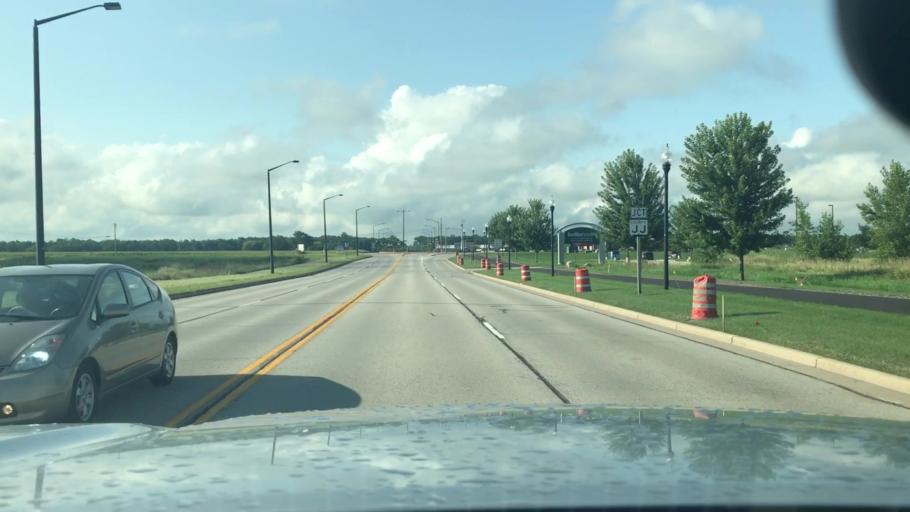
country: US
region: Wisconsin
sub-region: Brown County
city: Bellevue
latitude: 44.4681
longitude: -87.9173
